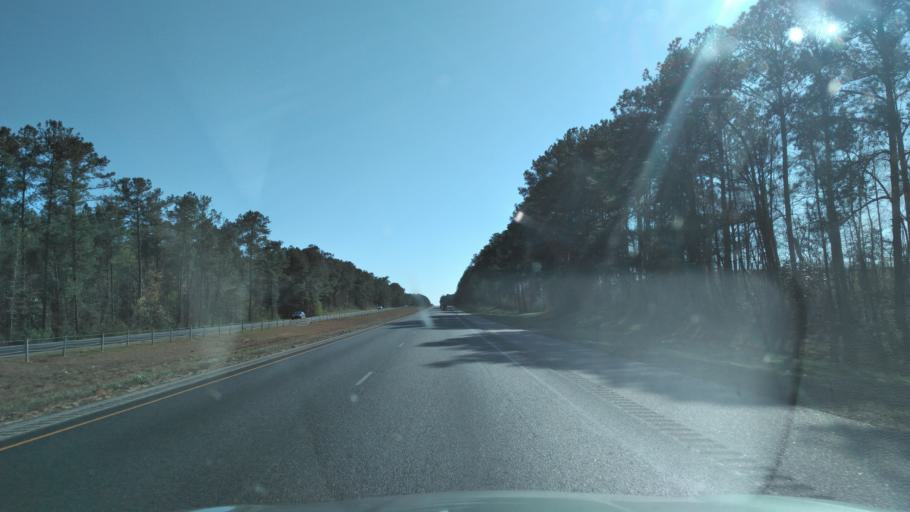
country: US
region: Alabama
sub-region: Butler County
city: Georgiana
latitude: 31.7257
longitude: -86.7237
